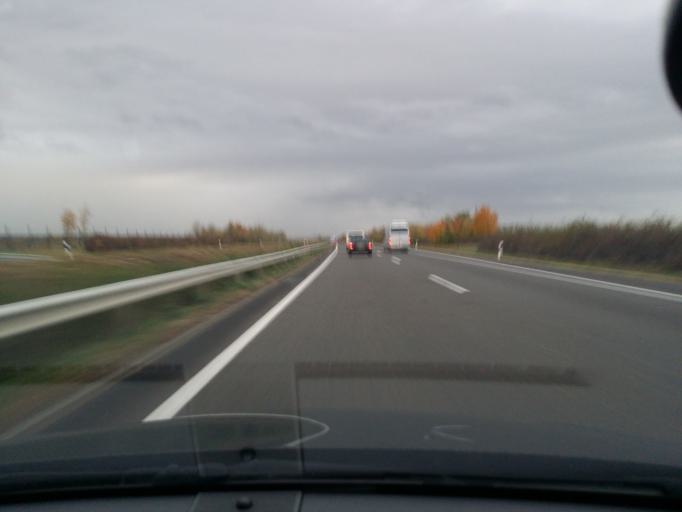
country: HU
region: Heves
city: Adacs
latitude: 47.7307
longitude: 19.9689
